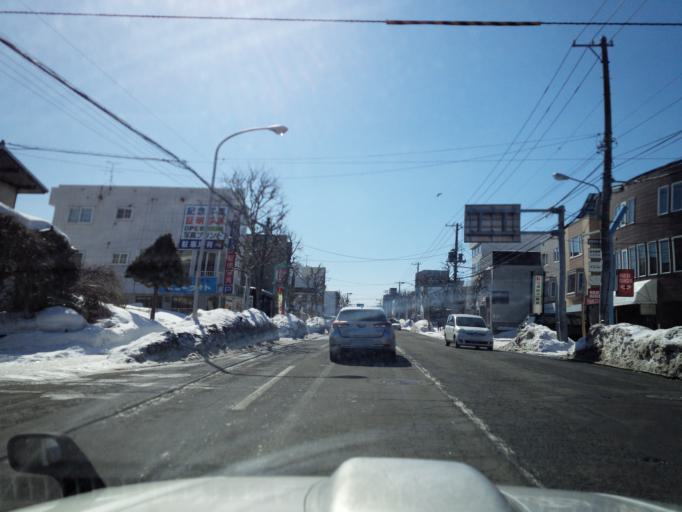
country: JP
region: Hokkaido
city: Sapporo
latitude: 43.0048
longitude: 141.4309
